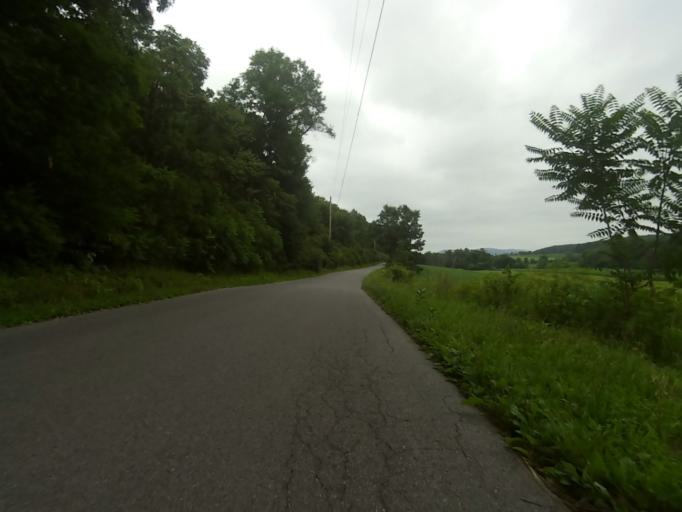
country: US
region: Pennsylvania
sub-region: Blair County
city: Tyrone
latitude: 40.6778
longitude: -78.1046
